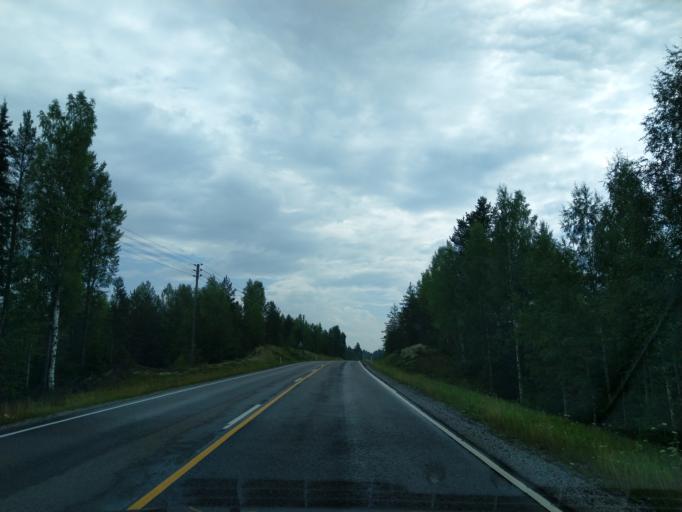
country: FI
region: South Karelia
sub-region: Imatra
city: Parikkala
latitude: 61.6415
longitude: 29.4261
